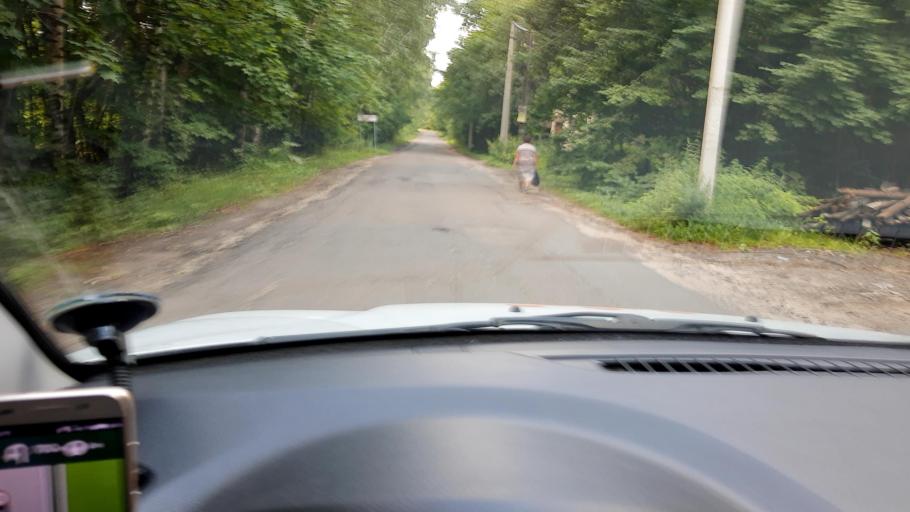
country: RU
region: Nizjnij Novgorod
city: Afonino
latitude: 56.2041
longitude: 44.0240
